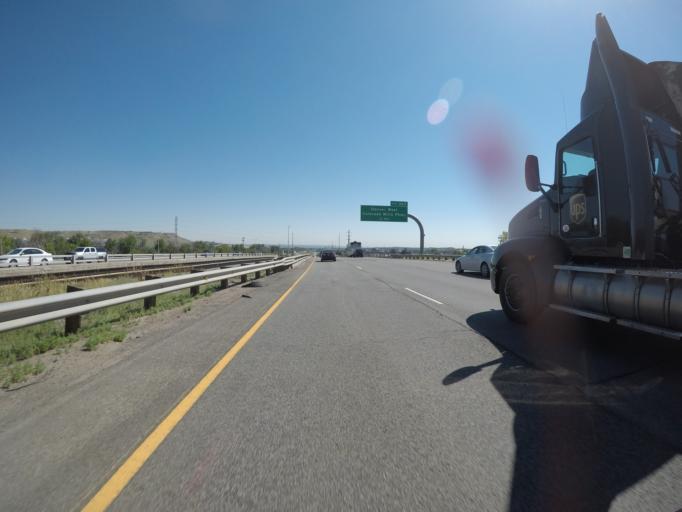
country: US
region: Colorado
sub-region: Jefferson County
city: West Pleasant View
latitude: 39.7303
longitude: -105.1712
